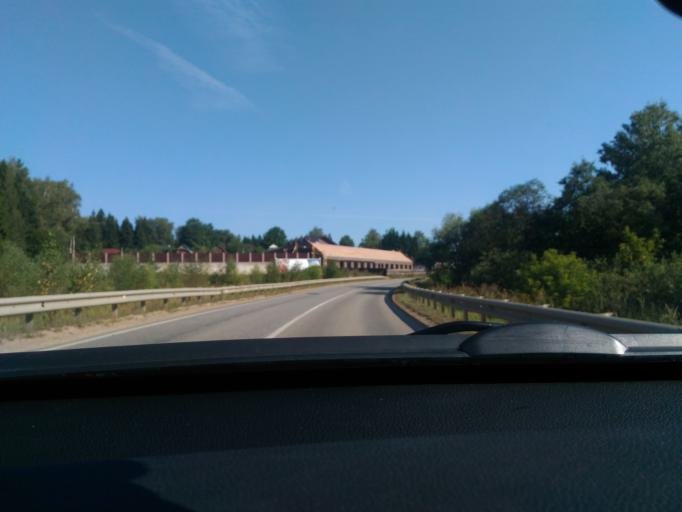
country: RU
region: Moskovskaya
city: Podosinki
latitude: 56.2122
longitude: 37.5429
